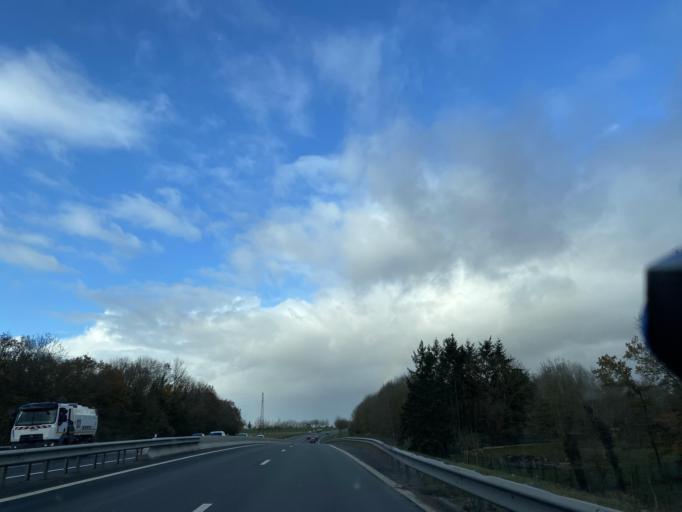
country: FR
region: Centre
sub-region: Departement d'Eure-et-Loir
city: Luce
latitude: 48.4265
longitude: 1.4345
